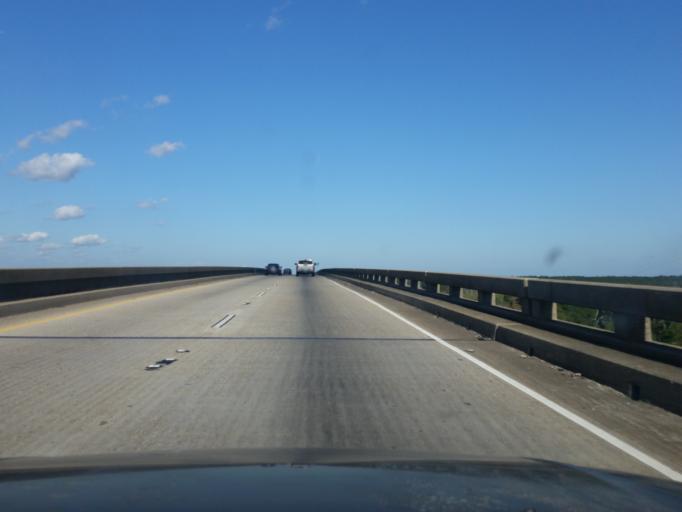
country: US
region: Mississippi
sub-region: Hancock County
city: Pearlington
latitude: 30.3030
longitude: -89.6432
